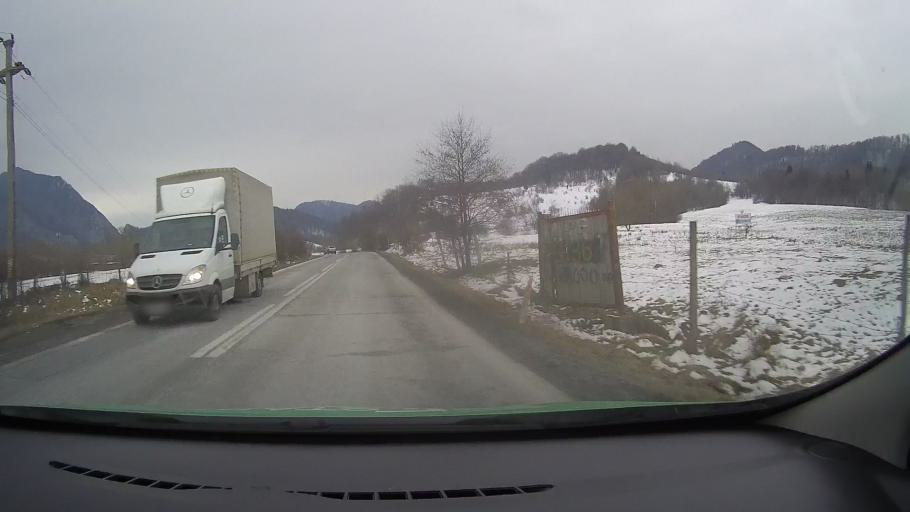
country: RO
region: Brasov
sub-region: Oras Rasnov
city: Rasnov
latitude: 45.5514
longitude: 25.4896
